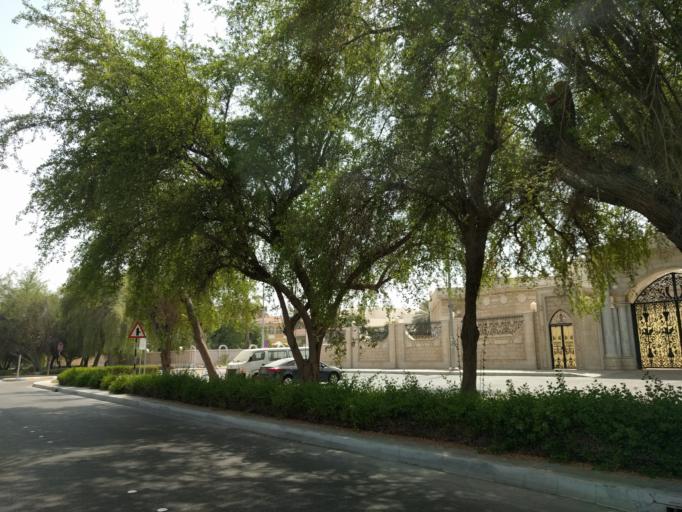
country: AE
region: Abu Dhabi
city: Abu Dhabi
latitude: 24.4440
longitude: 54.4191
